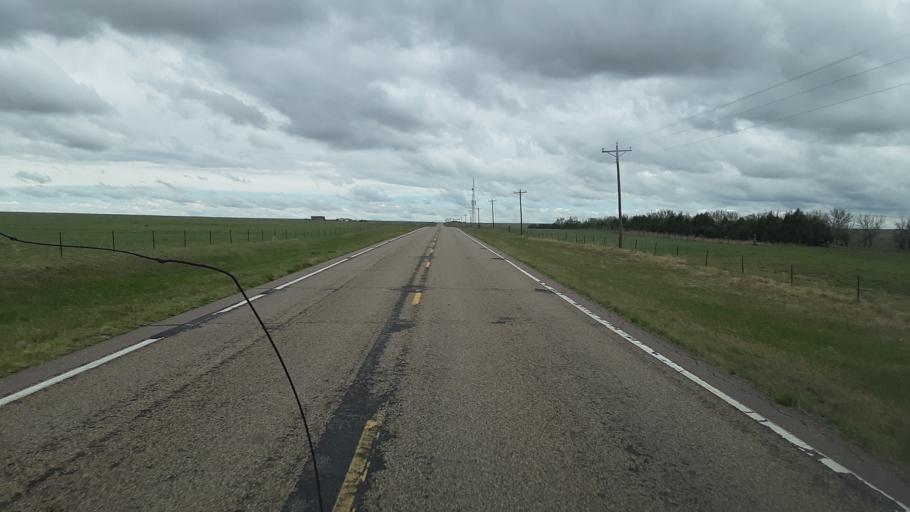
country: US
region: Colorado
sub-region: El Paso County
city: Ellicott
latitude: 38.8399
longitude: -104.0062
